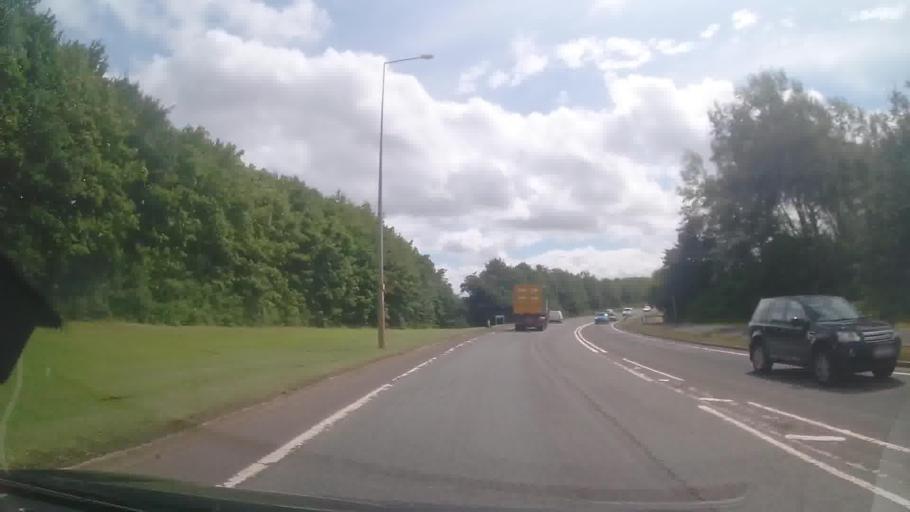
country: GB
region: England
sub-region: Shropshire
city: Shifnal
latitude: 52.6843
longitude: -2.4064
